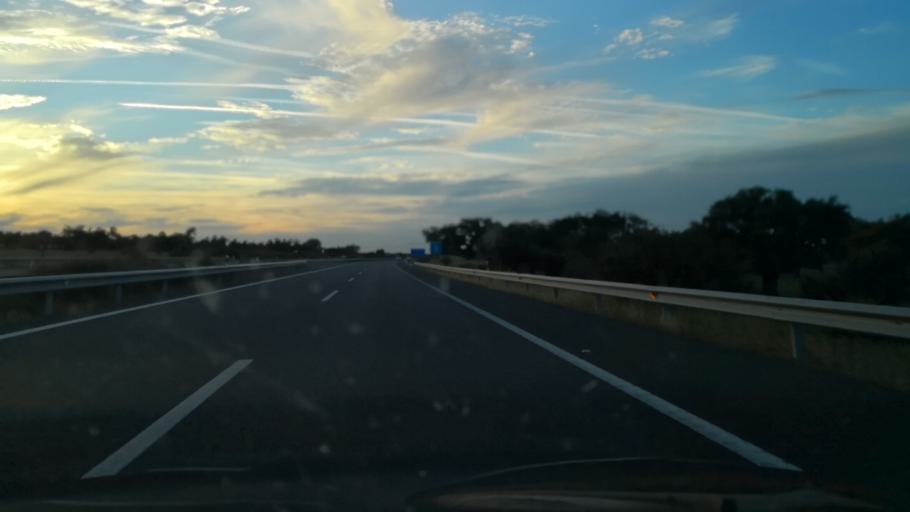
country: ES
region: Extremadura
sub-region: Provincia de Caceres
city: Casas de Don Antonio
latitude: 39.2202
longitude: -6.2944
